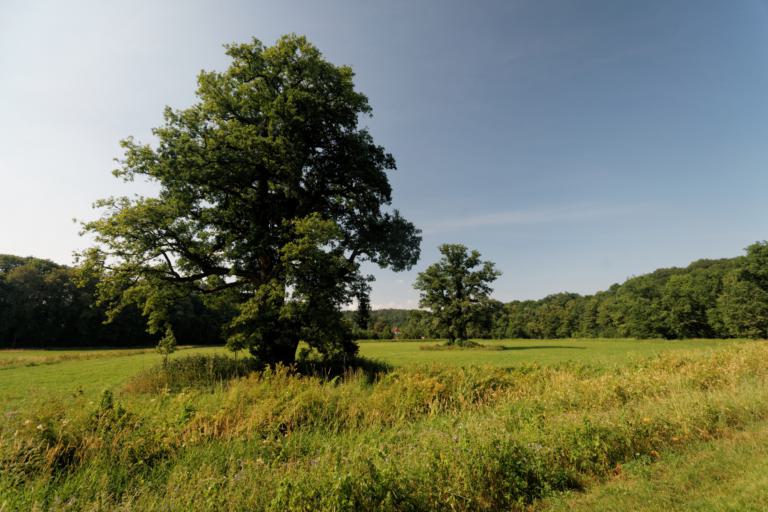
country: CZ
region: Kralovehradecky
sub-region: Okres Nachod
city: Ceska Skalice
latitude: 50.4176
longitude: 16.0576
